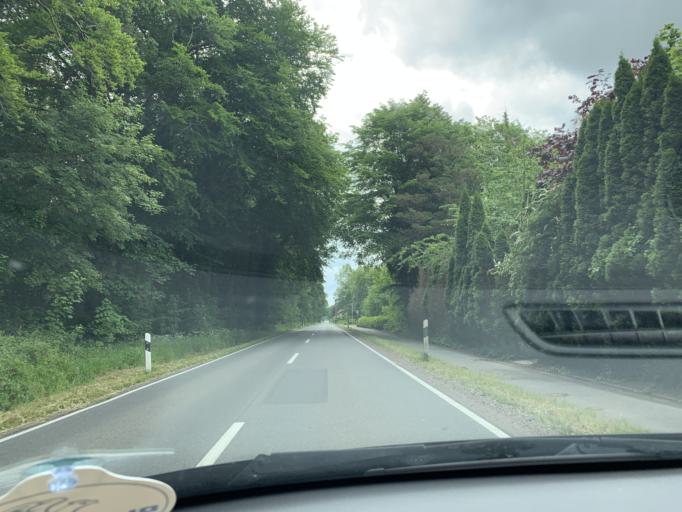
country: DE
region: Lower Saxony
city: Bockhorn
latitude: 53.3696
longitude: 8.0595
